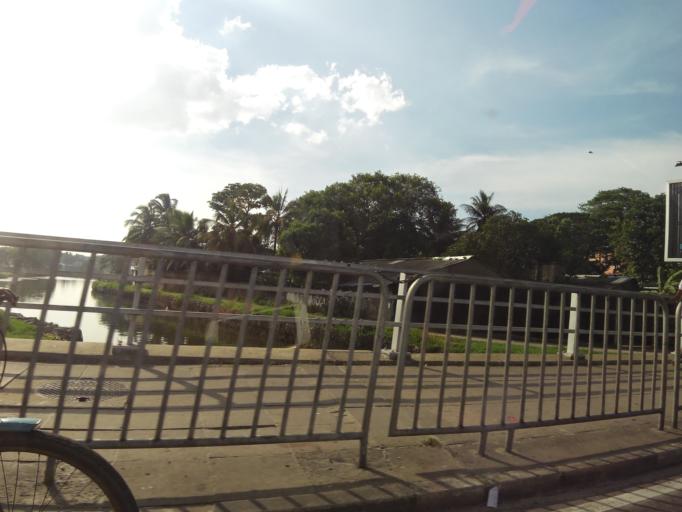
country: LK
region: Western
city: Kolonnawa
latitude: 6.9431
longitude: 79.8782
